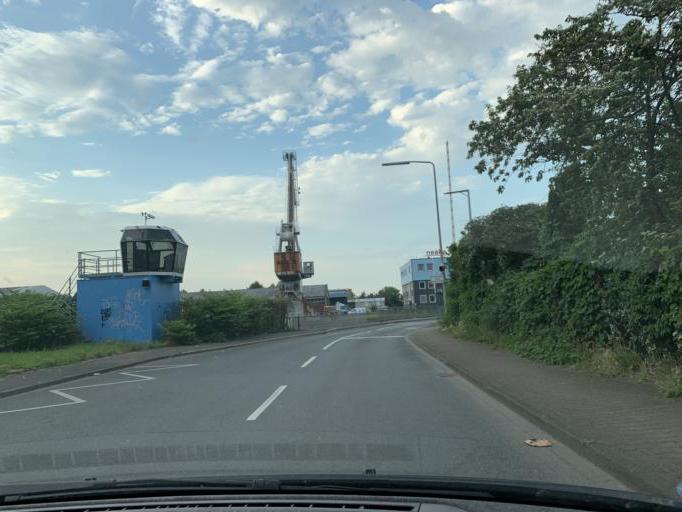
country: DE
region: North Rhine-Westphalia
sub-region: Regierungsbezirk Dusseldorf
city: Dusseldorf
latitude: 51.2200
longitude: 6.7435
